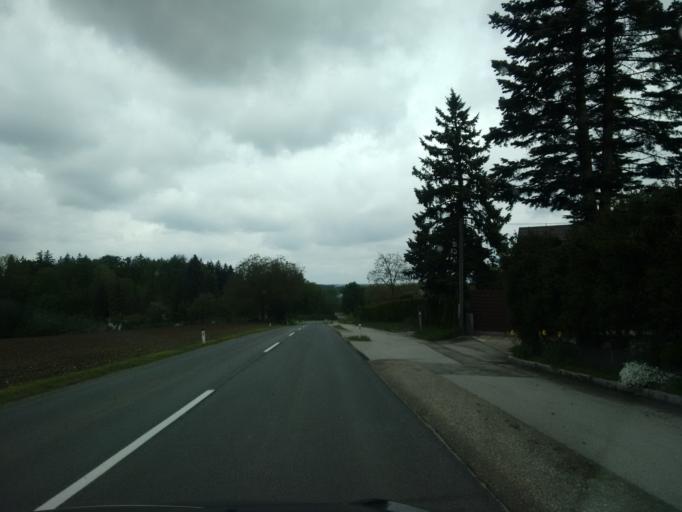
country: AT
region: Upper Austria
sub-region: Politischer Bezirk Steyr-Land
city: Waldneukirchen
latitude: 48.0040
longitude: 14.2554
